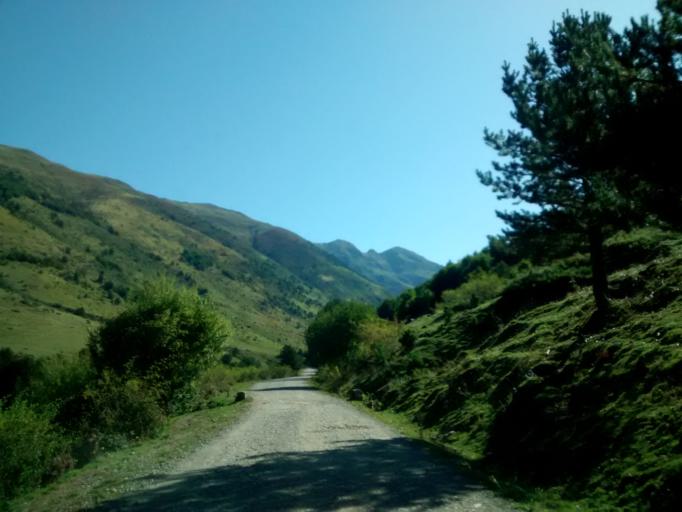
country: ES
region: Aragon
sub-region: Provincia de Huesca
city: Aragues del Puerto
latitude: 42.8531
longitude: -0.6855
